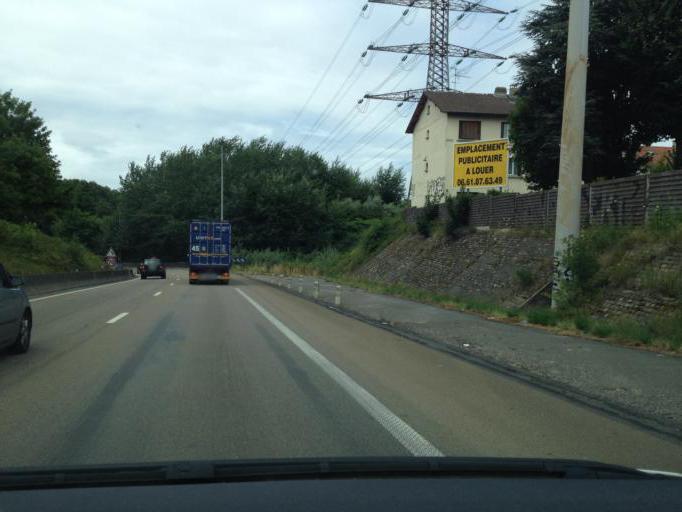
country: FR
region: Ile-de-France
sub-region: Departement de l'Essonne
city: Palaiseau
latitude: 48.7196
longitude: 2.2581
